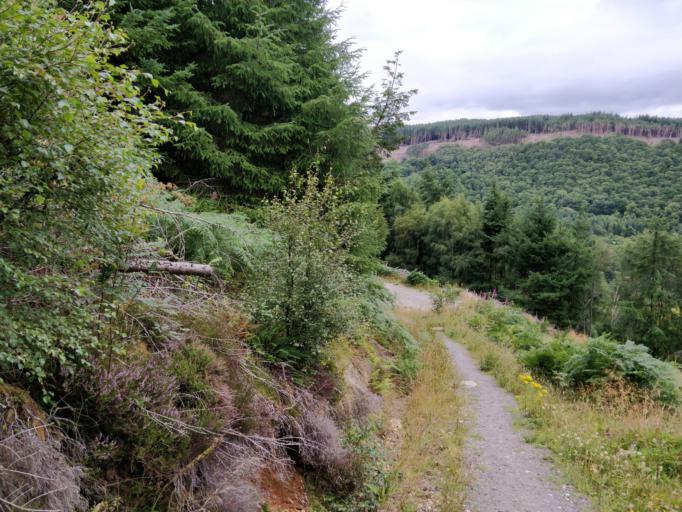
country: GB
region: Scotland
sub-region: Highland
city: Beauly
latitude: 57.2069
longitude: -4.6147
